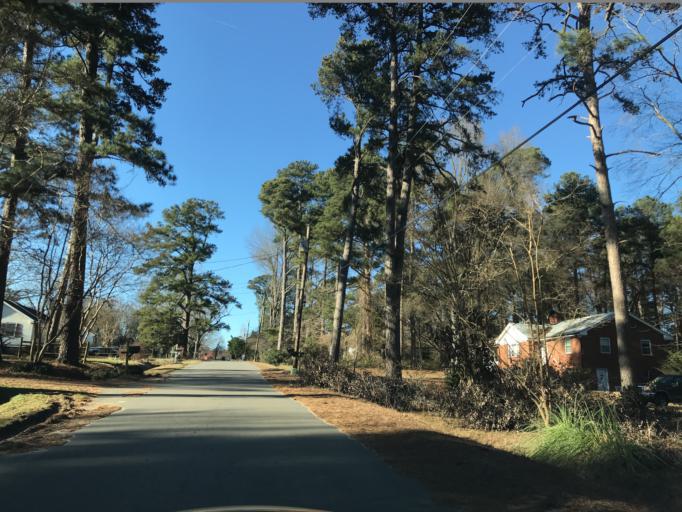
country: US
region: North Carolina
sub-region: Wake County
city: Raleigh
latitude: 35.8413
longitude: -78.6075
